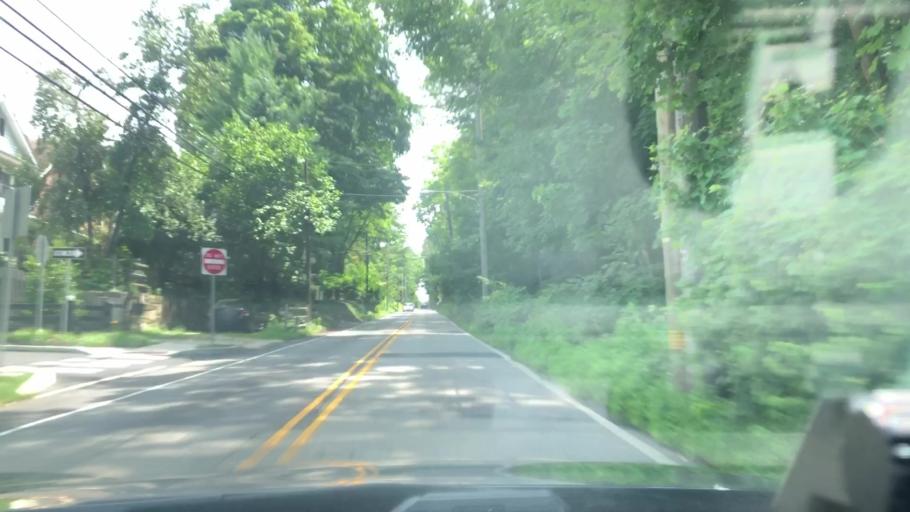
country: US
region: Pennsylvania
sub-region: Montgomery County
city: Flourtown
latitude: 40.0902
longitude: -75.2191
